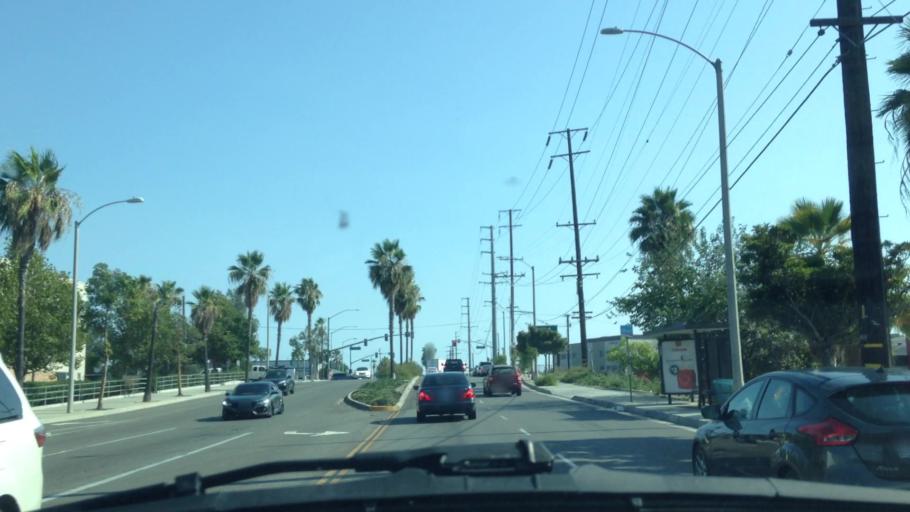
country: US
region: California
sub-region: Orange County
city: Fullerton
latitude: 33.8562
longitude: -117.9200
